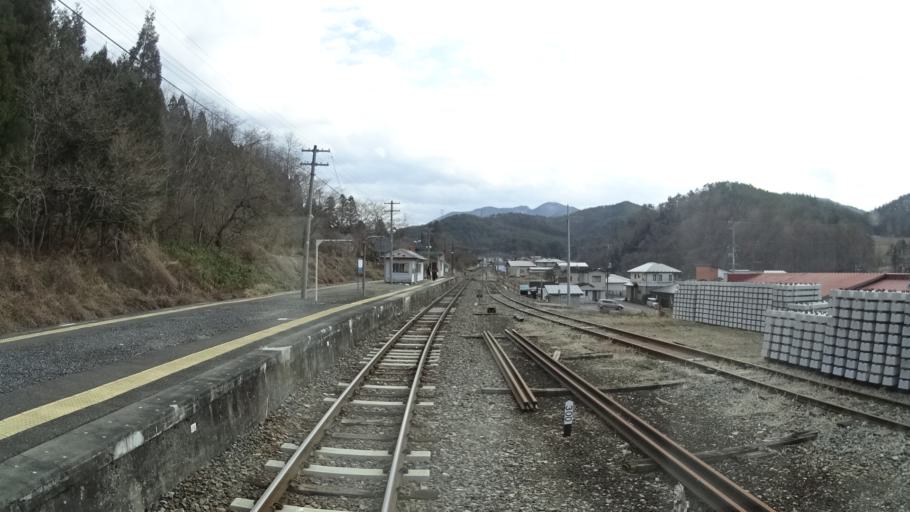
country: JP
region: Iwate
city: Tono
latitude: 39.3511
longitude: 141.3504
